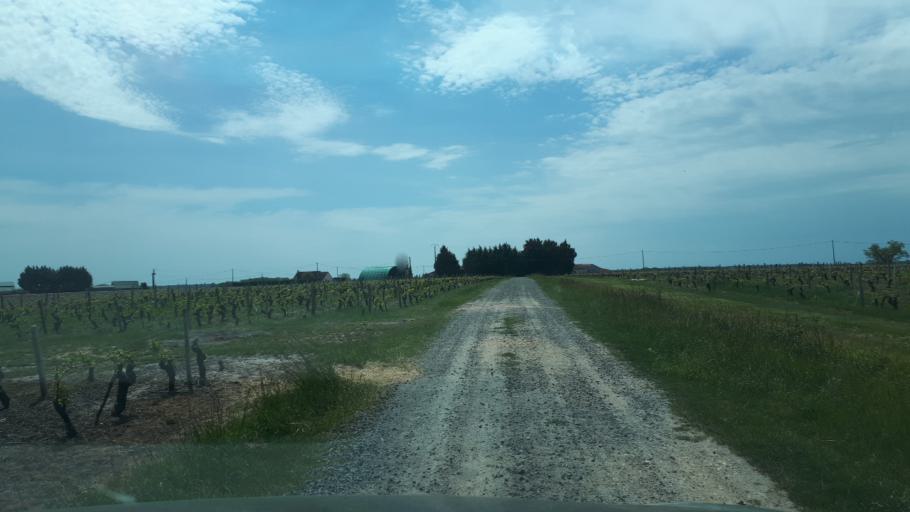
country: FR
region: Centre
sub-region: Departement du Loir-et-Cher
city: Saint-Romain-sur-Cher
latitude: 47.3557
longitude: 1.4298
